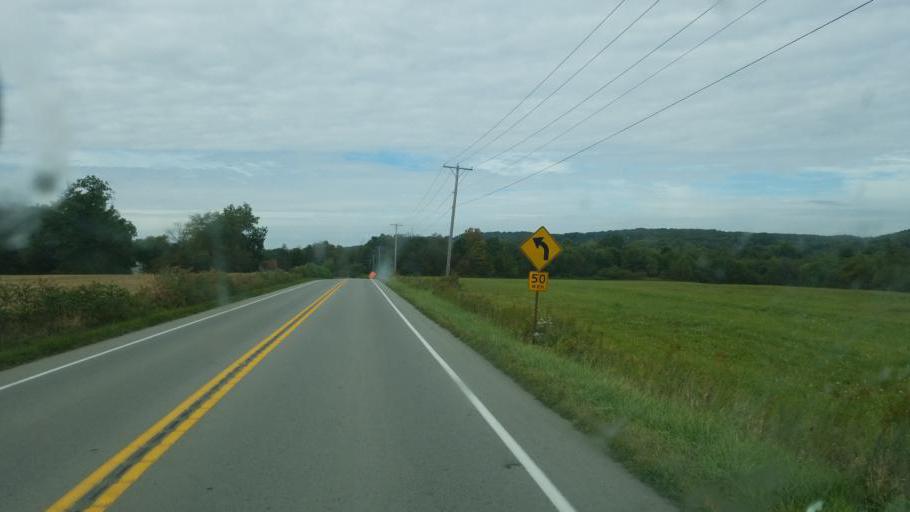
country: US
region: Pennsylvania
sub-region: Mercer County
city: Stoneboro
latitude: 41.4104
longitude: -80.2385
